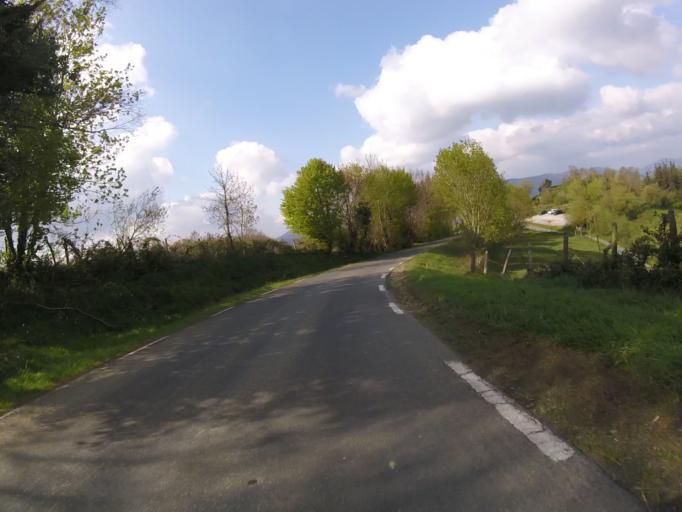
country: ES
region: Basque Country
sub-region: Provincia de Guipuzcoa
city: Azkoitia
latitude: 43.2076
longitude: -2.3349
